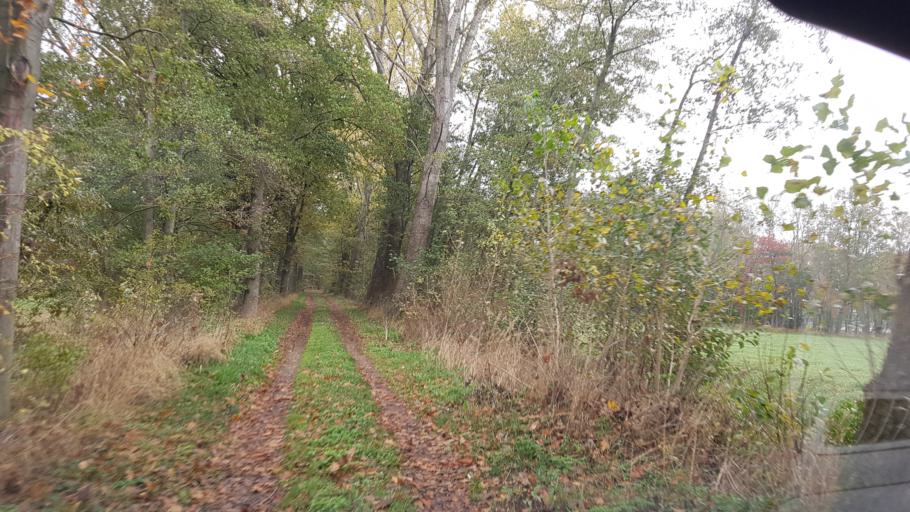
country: DE
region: Brandenburg
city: Schonewalde
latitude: 51.6924
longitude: 13.5993
